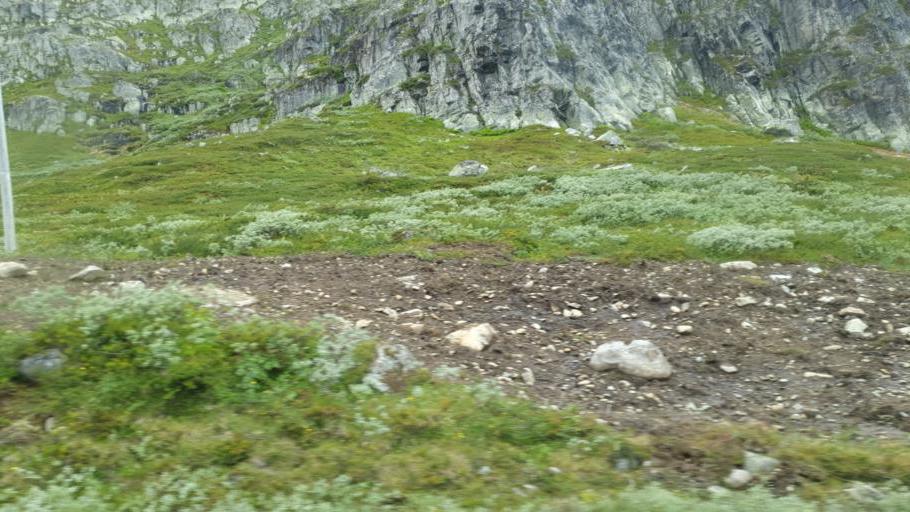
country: NO
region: Oppland
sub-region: Vestre Slidre
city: Slidre
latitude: 61.3085
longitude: 8.8068
